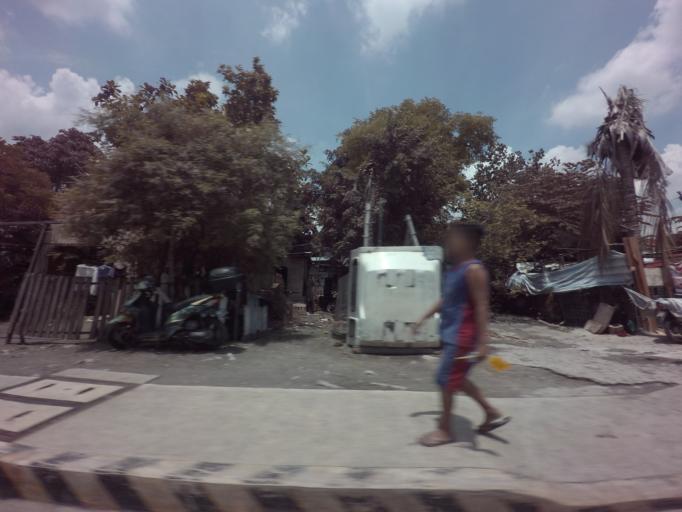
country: PH
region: Calabarzon
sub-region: Province of Laguna
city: San Pedro
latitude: 14.3861
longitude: 121.0507
